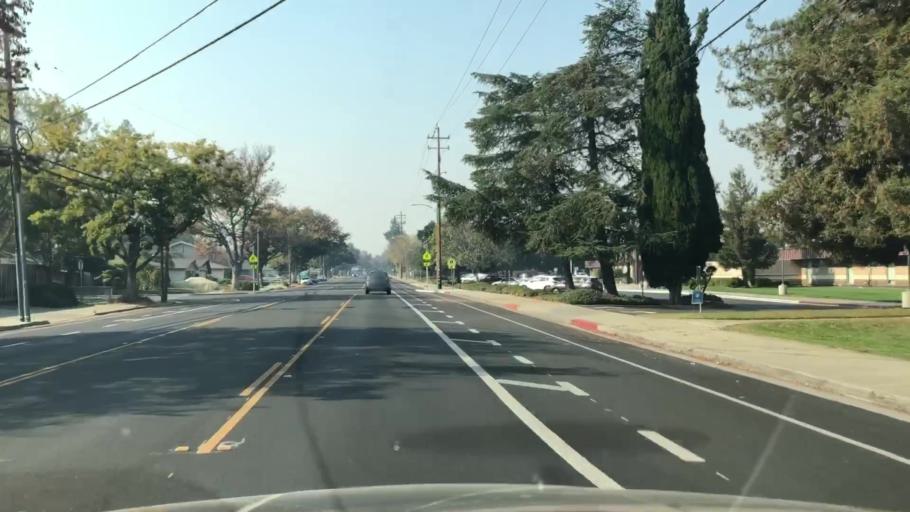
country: US
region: California
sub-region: Santa Clara County
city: Campbell
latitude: 37.3033
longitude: -121.9849
